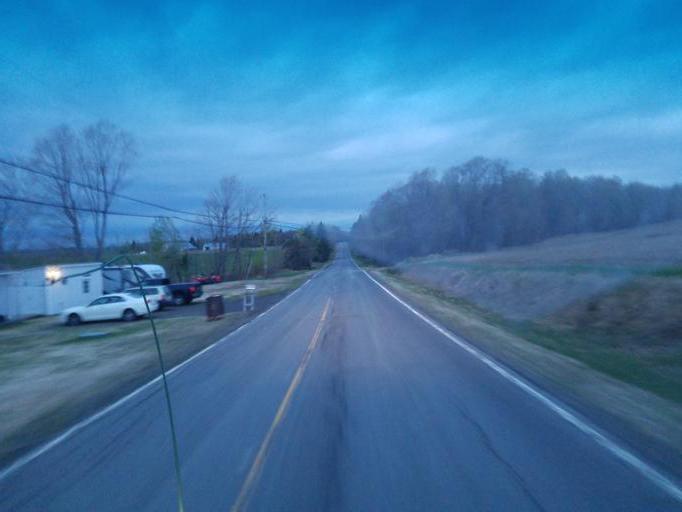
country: US
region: Maine
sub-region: Aroostook County
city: Caribou
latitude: 46.8702
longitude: -68.2115
